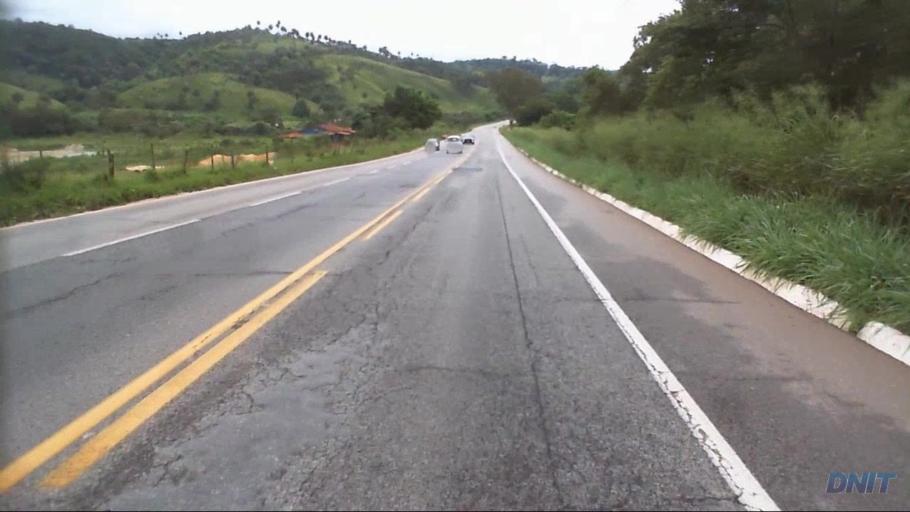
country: BR
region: Minas Gerais
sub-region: Barao De Cocais
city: Barao de Cocais
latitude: -19.8182
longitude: -43.3939
